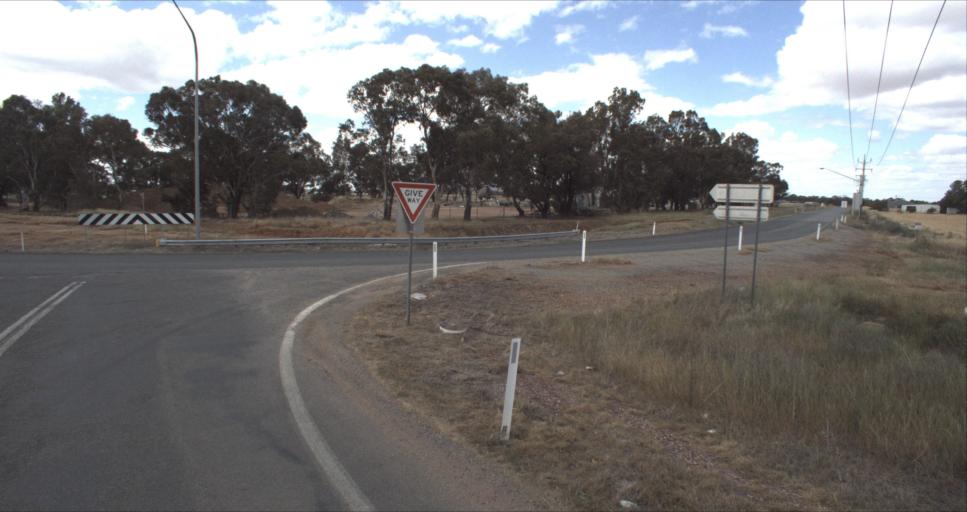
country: AU
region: New South Wales
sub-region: Leeton
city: Leeton
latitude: -34.5716
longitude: 146.3945
